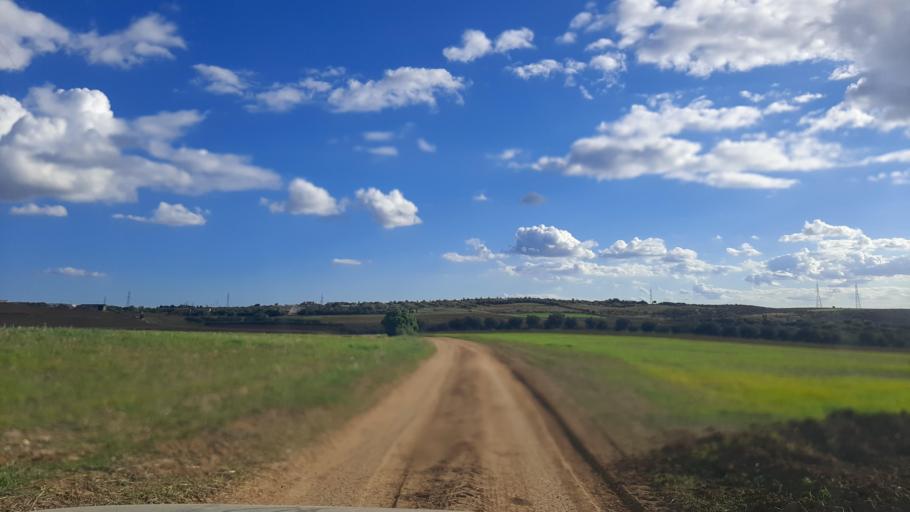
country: TN
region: Nabul
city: Bu `Urqub
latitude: 36.4475
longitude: 10.5015
